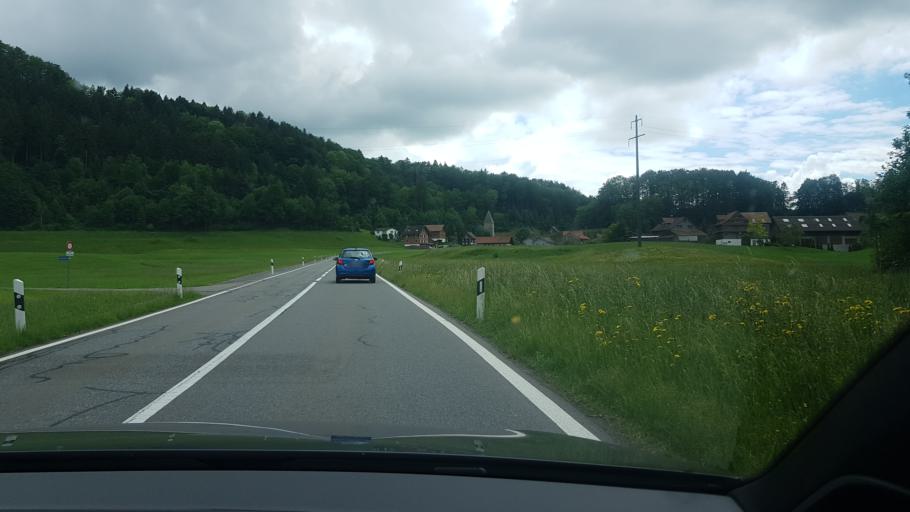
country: CH
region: Schwyz
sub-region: Bezirk Schwyz
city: Sattel
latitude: 47.0962
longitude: 8.6339
